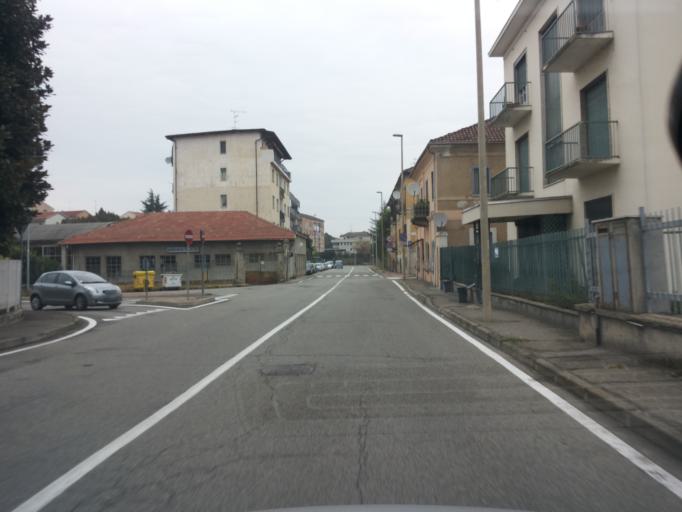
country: IT
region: Piedmont
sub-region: Provincia di Vercelli
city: Vercelli
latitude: 45.3263
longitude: 8.4349
